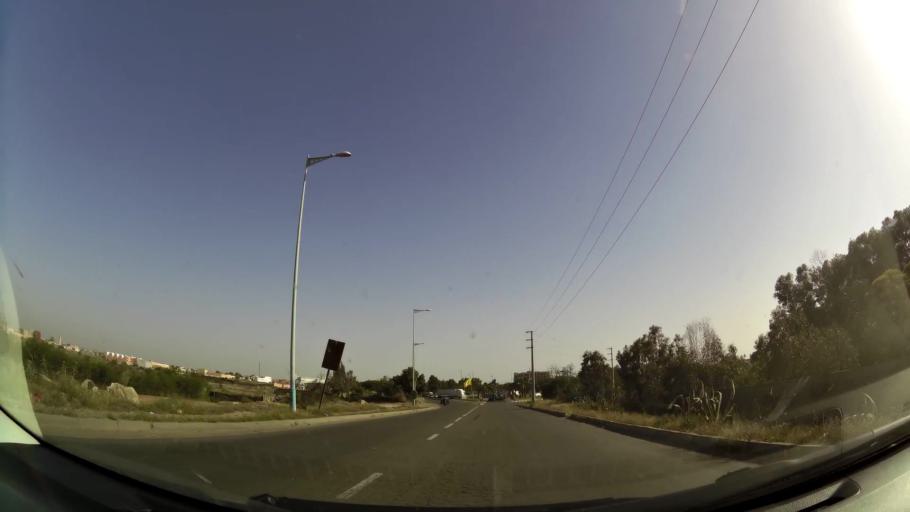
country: MA
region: Souss-Massa-Draa
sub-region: Inezgane-Ait Mellou
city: Inezgane
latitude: 30.3537
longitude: -9.5060
